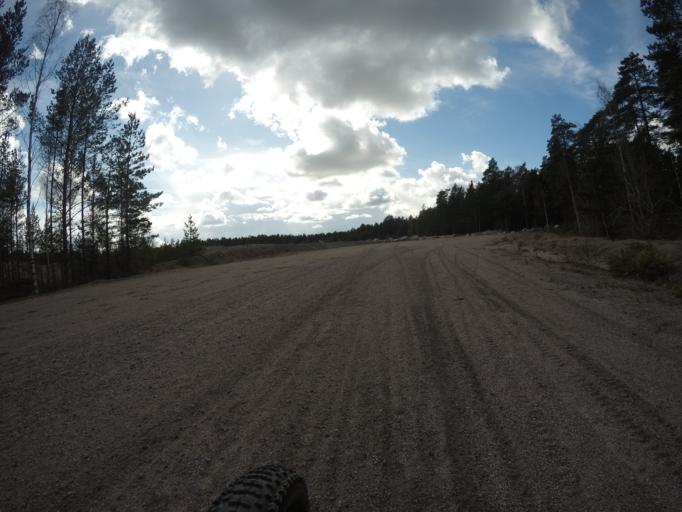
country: SE
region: Vaestmanland
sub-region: Kungsors Kommun
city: Kungsoer
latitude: 59.3746
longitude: 16.1062
